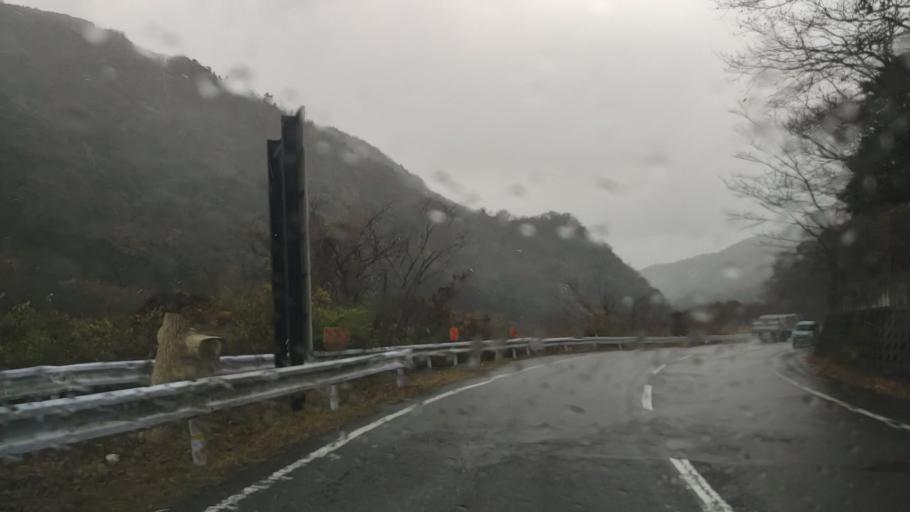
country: JP
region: Tokushima
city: Kamojimacho-jogejima
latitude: 34.1465
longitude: 134.3550
